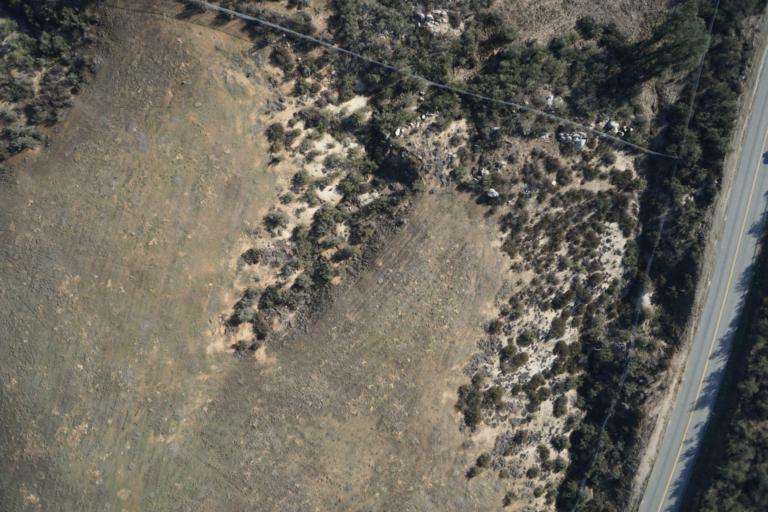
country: US
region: California
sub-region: Riverside County
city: East Hemet
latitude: 33.6135
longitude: -116.9266
